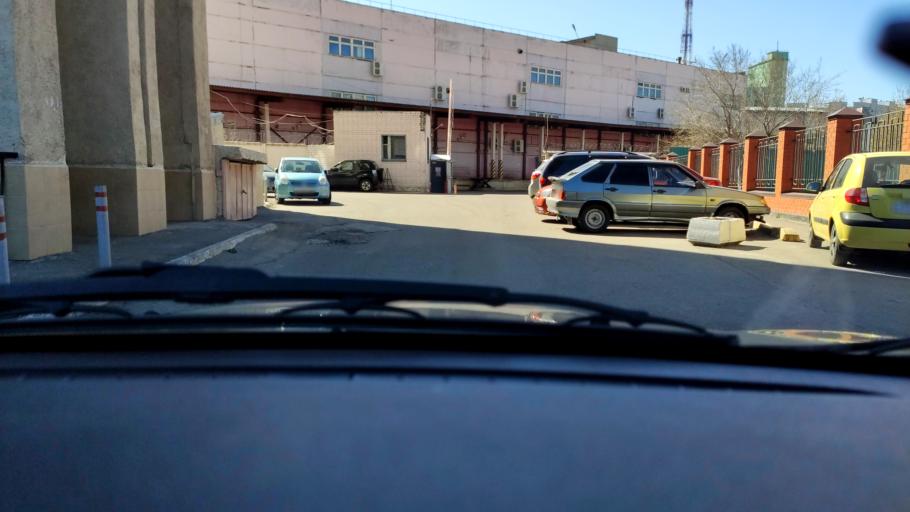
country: RU
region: Voronezj
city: Voronezh
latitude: 51.6777
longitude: 39.2016
